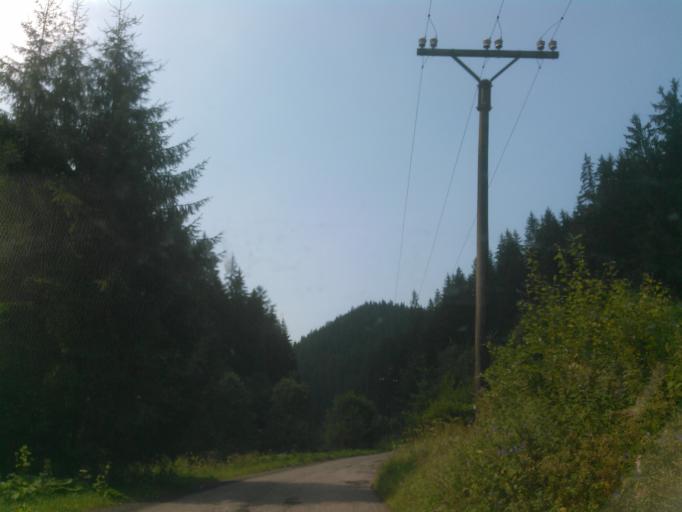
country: SK
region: Zilinsky
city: Ruzomberok
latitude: 48.9747
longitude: 19.4194
